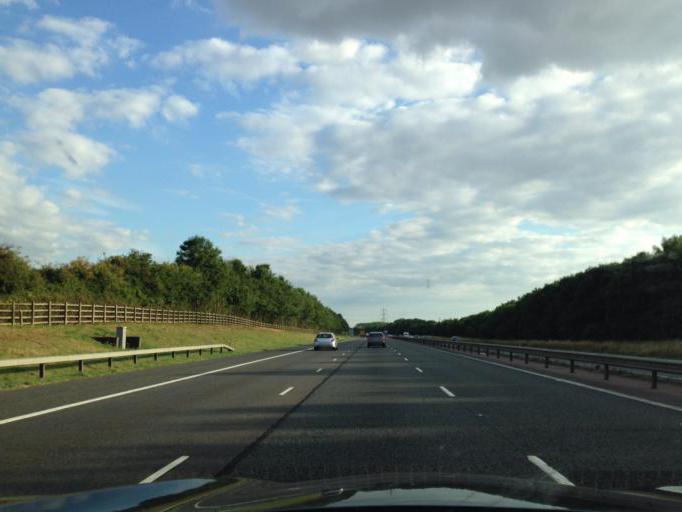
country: GB
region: England
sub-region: Oxfordshire
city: Wheatley
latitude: 51.7648
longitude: -1.1038
